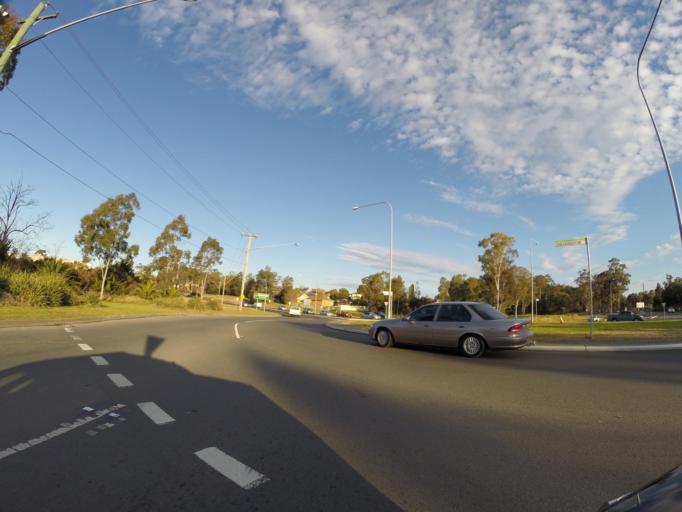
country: AU
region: New South Wales
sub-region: Fairfield
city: Horsley Park
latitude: -33.8509
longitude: 150.8768
